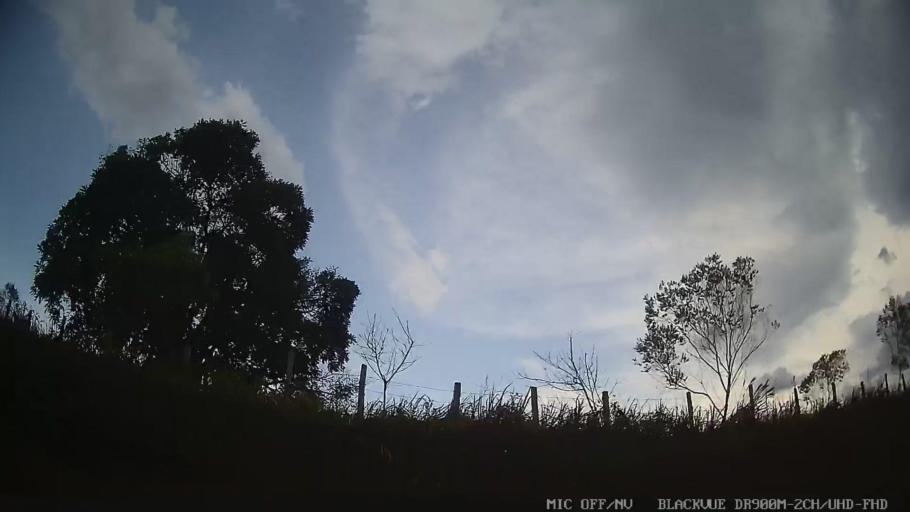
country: BR
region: Sao Paulo
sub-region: Itatiba
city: Itatiba
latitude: -22.9321
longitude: -46.7916
